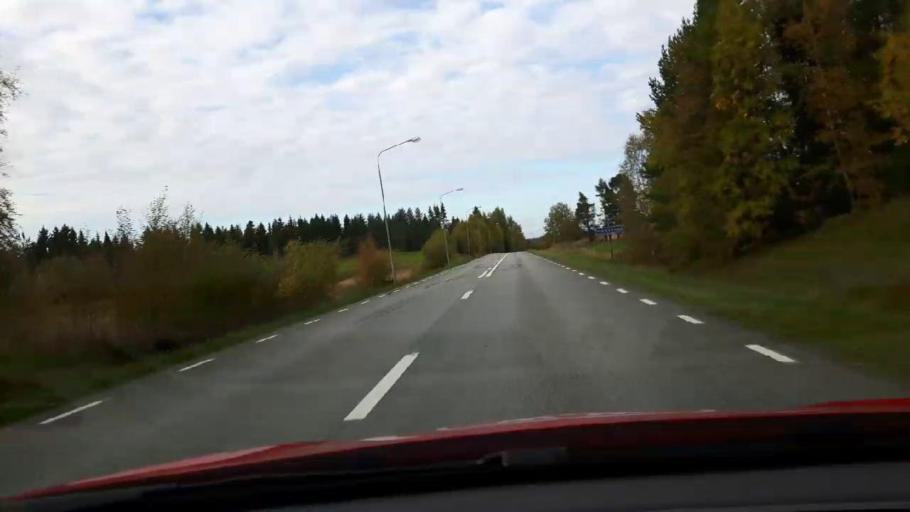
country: SE
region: Jaemtland
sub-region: Krokoms Kommun
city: Valla
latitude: 63.2383
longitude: 14.0048
